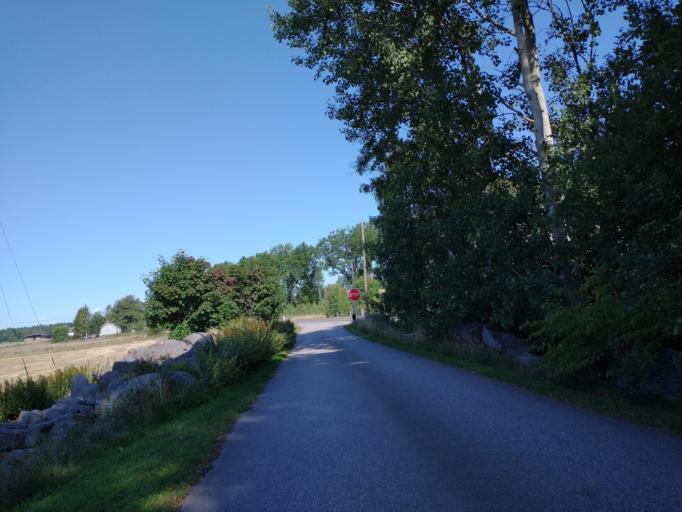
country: SE
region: Kalmar
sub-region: Kalmar Kommun
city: Lindsdal
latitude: 56.7873
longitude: 16.2646
